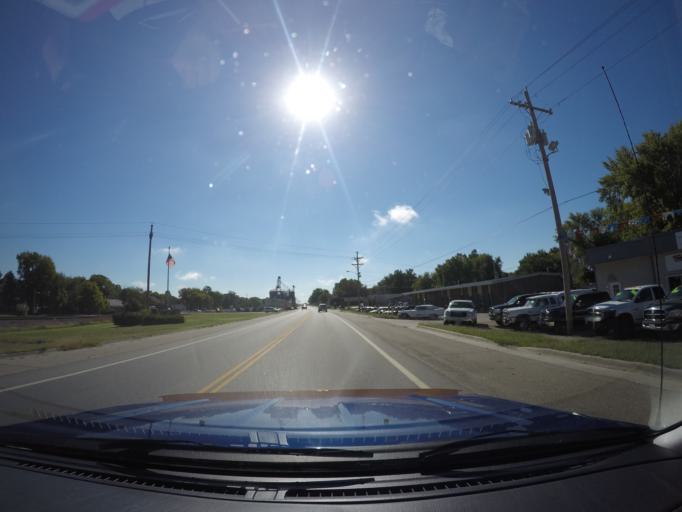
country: US
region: Kansas
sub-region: Shawnee County
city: Rossville
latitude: 39.1374
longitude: -95.9548
